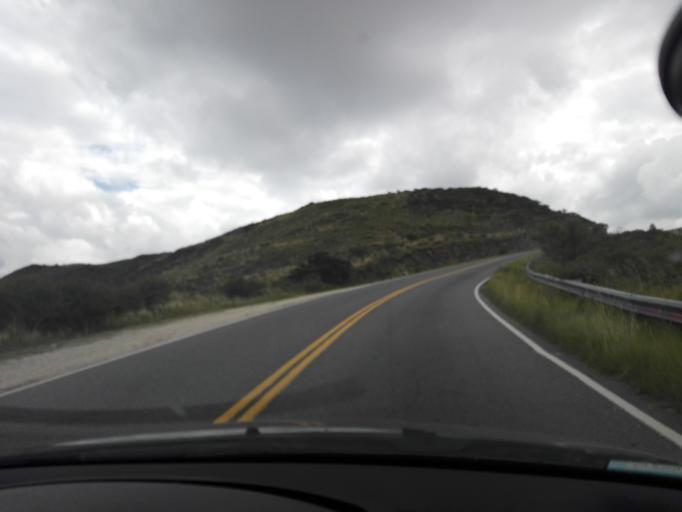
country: AR
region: Cordoba
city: Cuesta Blanca
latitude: -31.5954
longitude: -64.5357
